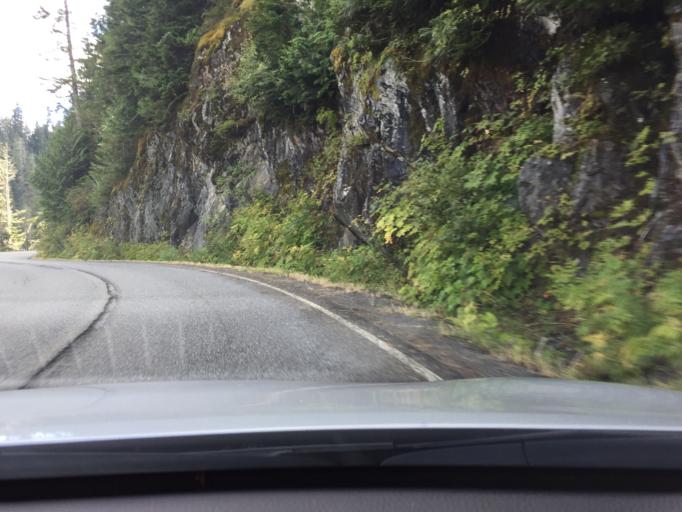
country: CA
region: British Columbia
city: Agassiz
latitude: 48.8691
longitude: -121.6607
